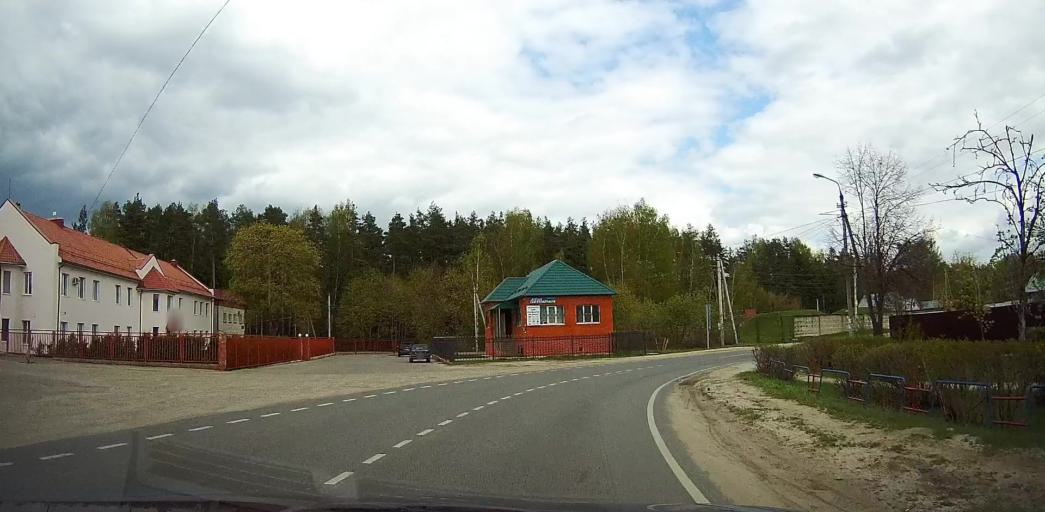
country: RU
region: Moskovskaya
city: Ashitkovo
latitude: 55.4381
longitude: 38.5794
